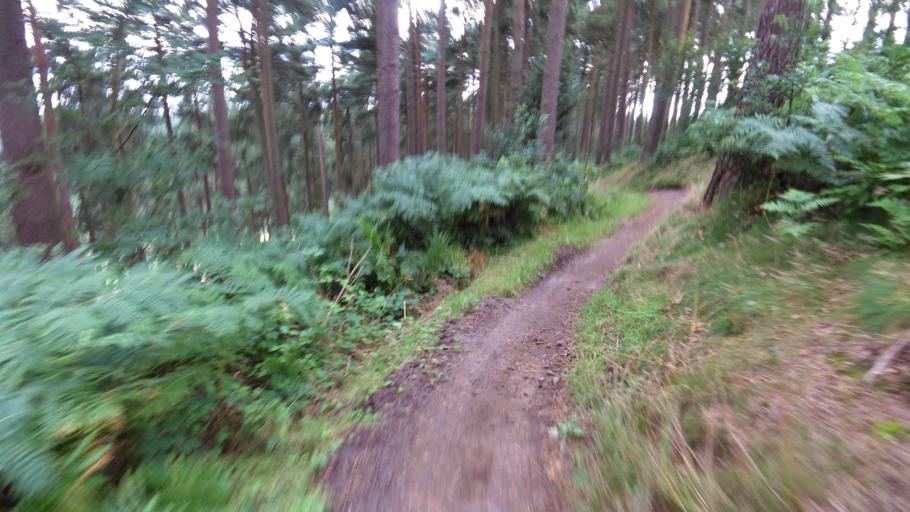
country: GB
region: England
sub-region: North Yorkshire
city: Thornton Dale
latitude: 54.2842
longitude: -0.6838
